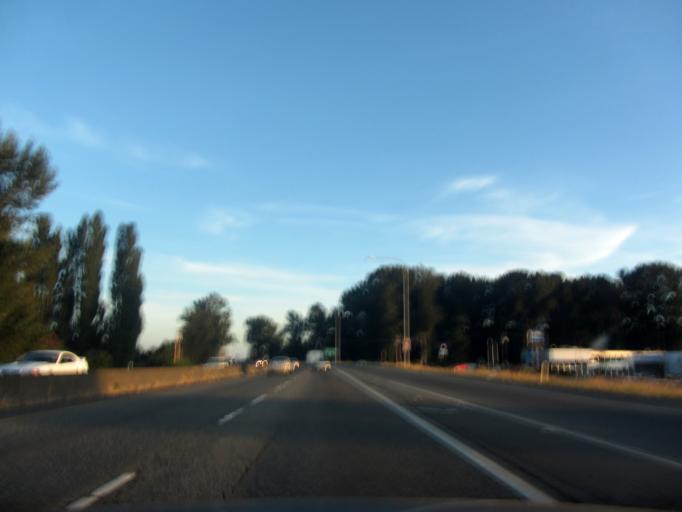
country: US
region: Washington
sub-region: Skagit County
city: Mount Vernon
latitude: 48.4319
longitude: -122.3411
